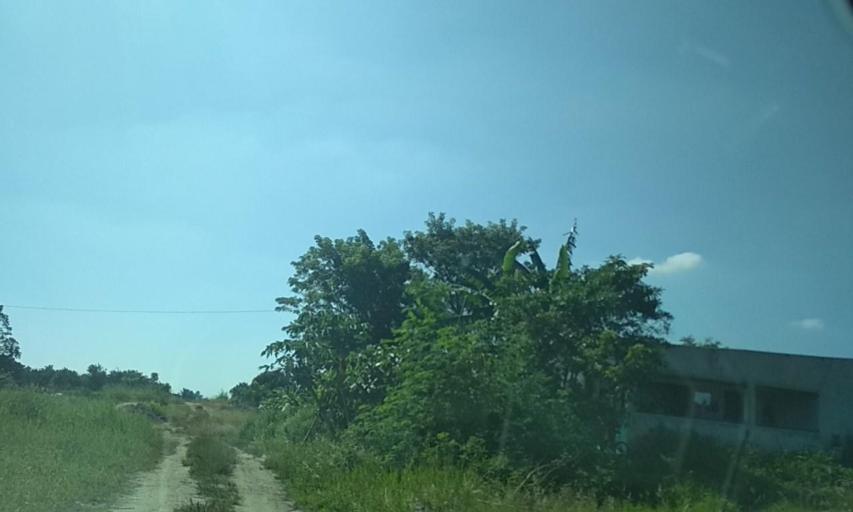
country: MX
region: Veracruz
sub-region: Martinez de la Torre
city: La Union Paso Largo
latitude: 20.1442
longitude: -97.0018
